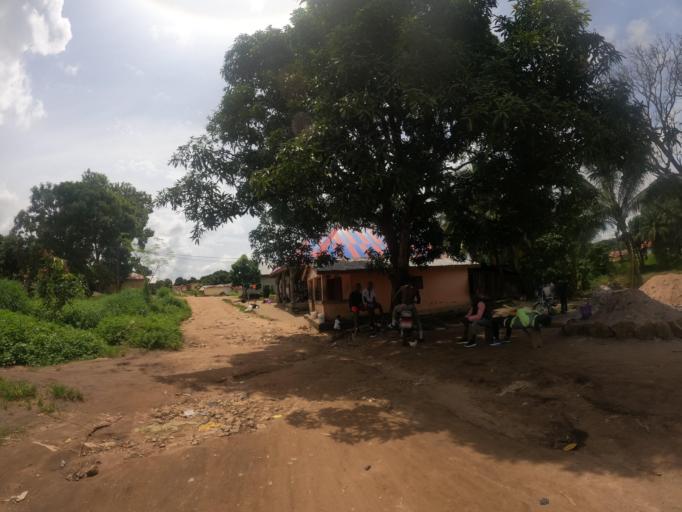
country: SL
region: Northern Province
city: Makeni
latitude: 8.8998
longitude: -12.0561
